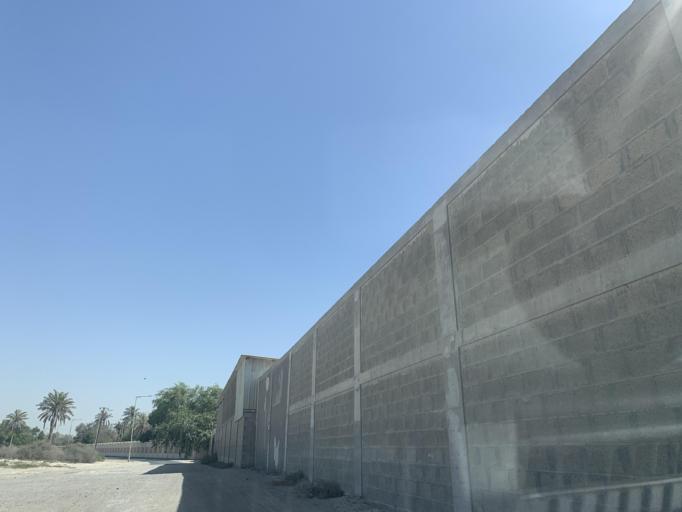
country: BH
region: Manama
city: Jidd Hafs
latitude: 26.2290
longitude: 50.4980
